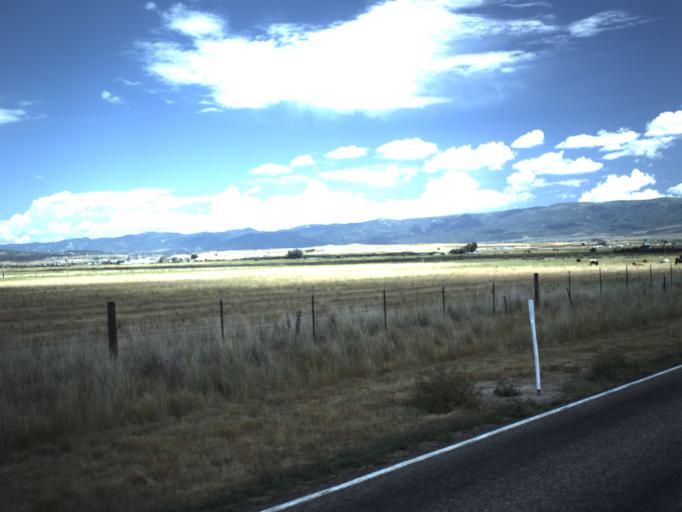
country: US
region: Utah
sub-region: Sanpete County
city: Moroni
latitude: 39.4755
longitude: -111.6086
